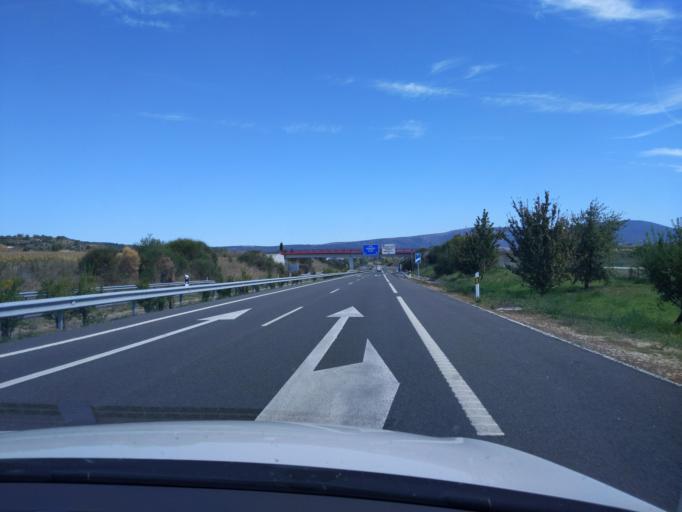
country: ES
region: Navarre
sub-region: Provincia de Navarra
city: Obanos
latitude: 42.6922
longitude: -1.7960
